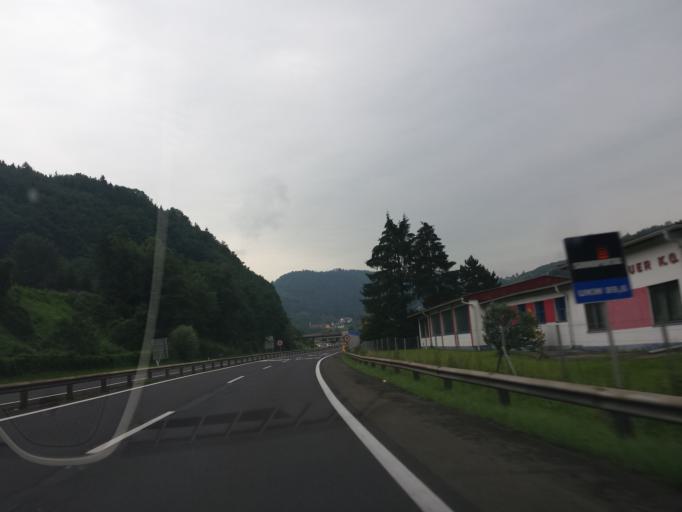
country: AT
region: Styria
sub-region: Politischer Bezirk Bruck-Muerzzuschlag
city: Bruck an der Mur
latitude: 47.3995
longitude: 15.2845
